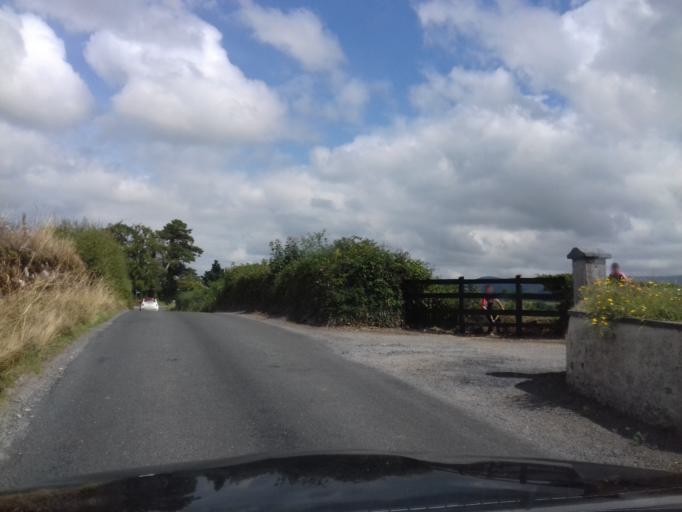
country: IE
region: Leinster
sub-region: Kilkenny
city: Graiguenamanagh
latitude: 52.6061
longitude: -6.9039
